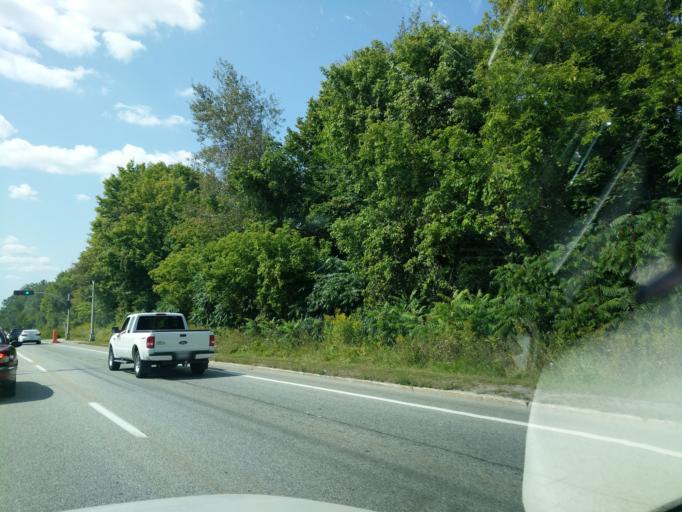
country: CA
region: Quebec
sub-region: Outaouais
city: Gatineau
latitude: 45.4454
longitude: -75.7724
